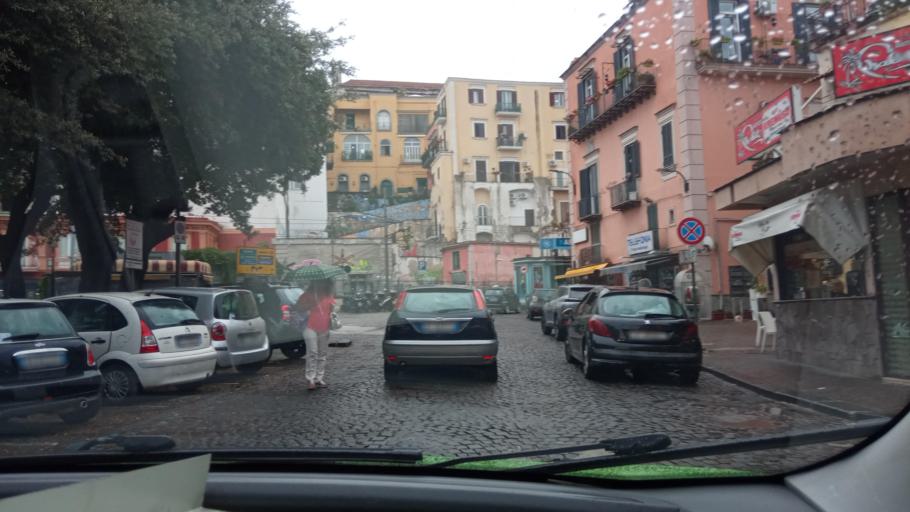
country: IT
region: Campania
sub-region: Provincia di Napoli
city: Pozzuoli
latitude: 40.8238
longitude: 14.1211
